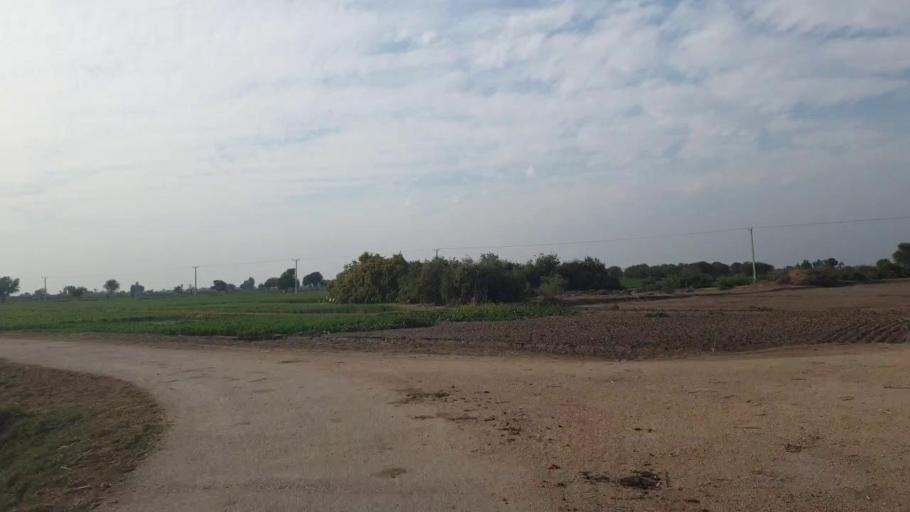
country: PK
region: Sindh
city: Shahdadpur
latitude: 26.0406
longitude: 68.5311
